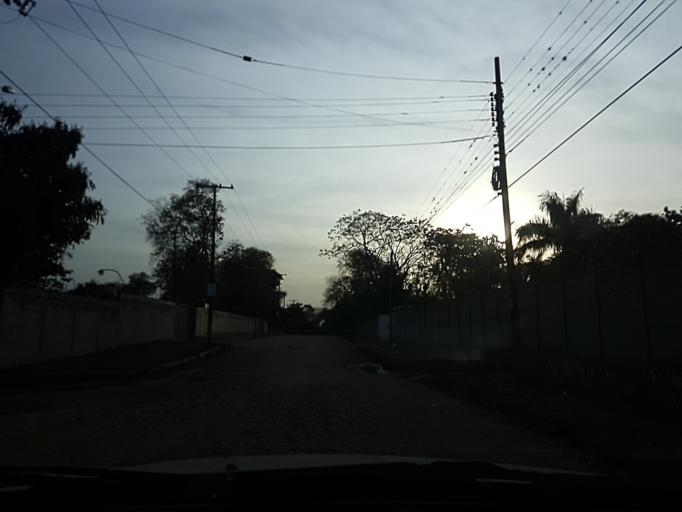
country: PY
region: Central
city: Colonia Mariano Roque Alonso
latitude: -25.2037
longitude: -57.5455
